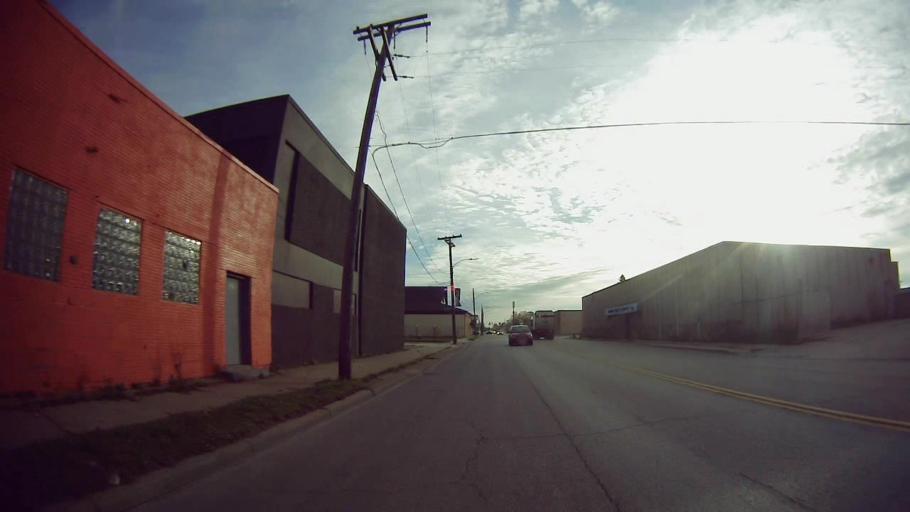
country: US
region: Michigan
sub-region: Wayne County
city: Highland Park
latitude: 42.4324
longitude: -83.0987
